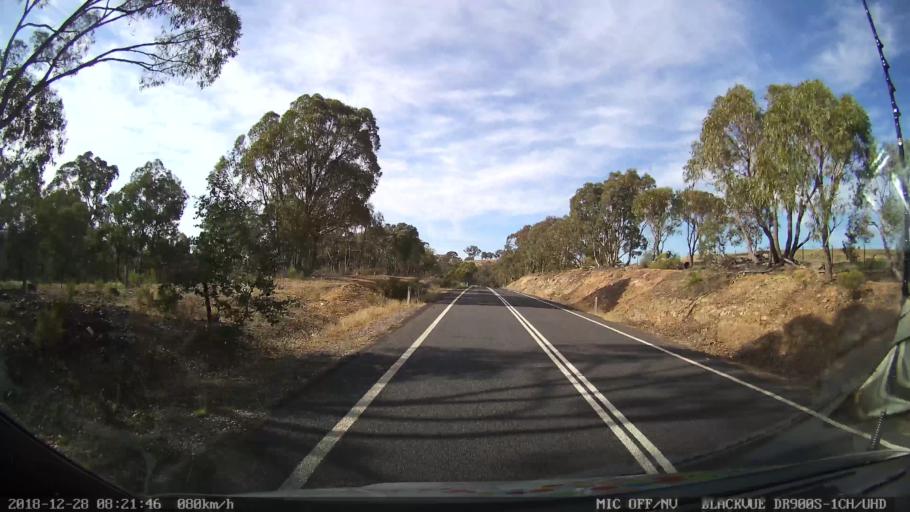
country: AU
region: New South Wales
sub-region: Blayney
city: Blayney
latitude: -33.8865
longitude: 149.3488
